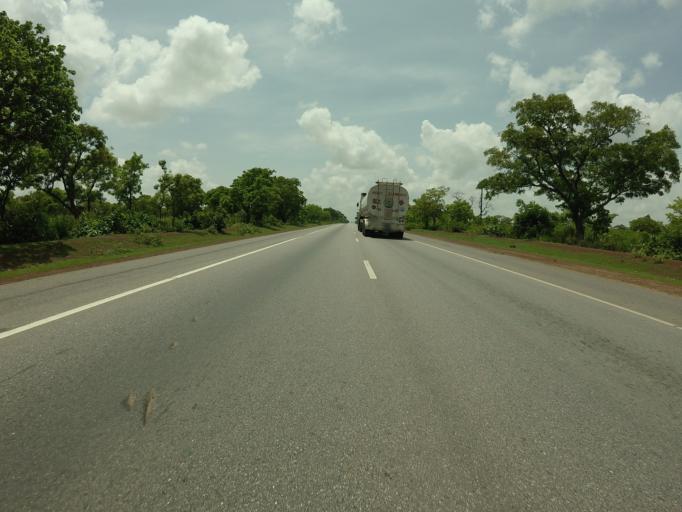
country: GH
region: Northern
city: Tamale
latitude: 9.2817
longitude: -0.9856
